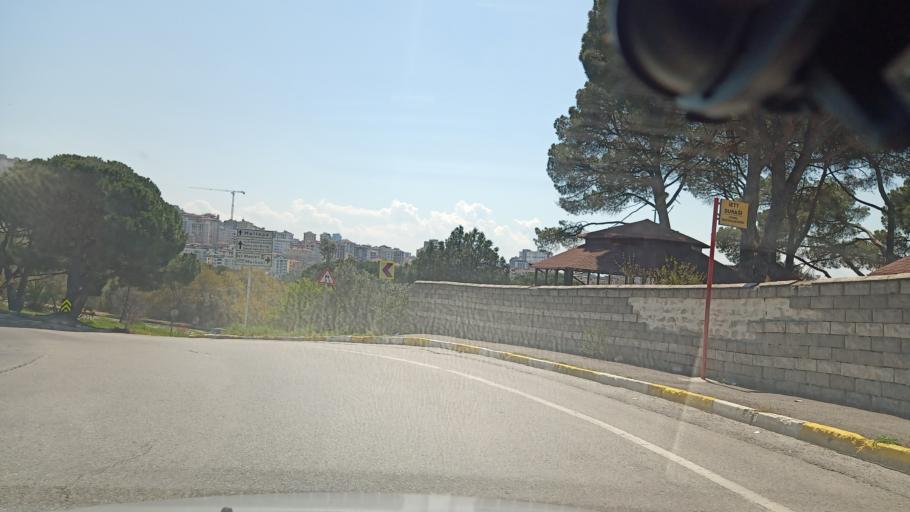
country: TR
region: Istanbul
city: Maltepe
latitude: 40.9486
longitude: 29.1423
